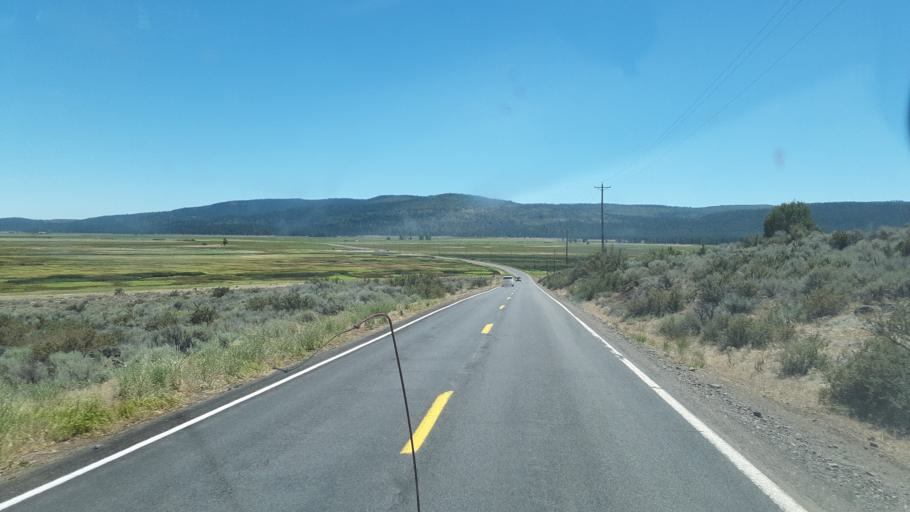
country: US
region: California
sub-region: Lassen County
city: Susanville
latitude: 40.5713
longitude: -120.6421
